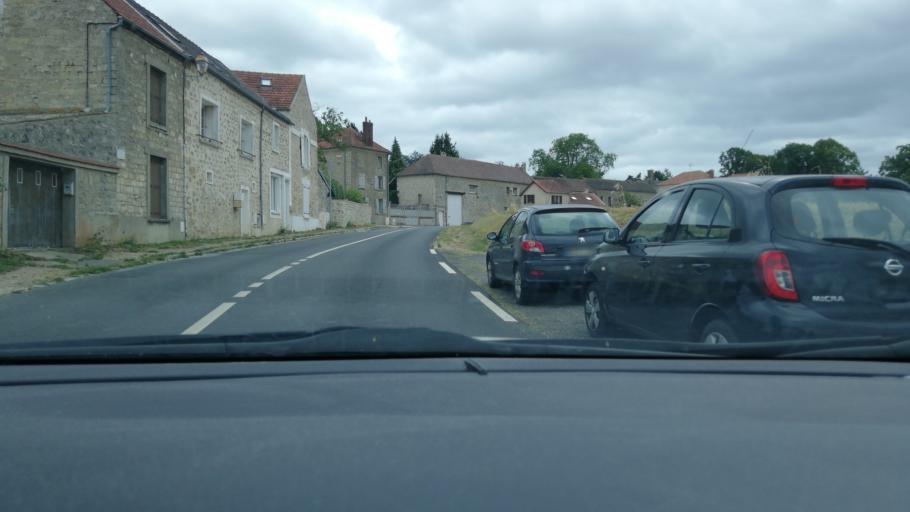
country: FR
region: Ile-de-France
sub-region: Departement du Val-d'Oise
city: Ennery
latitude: 49.1037
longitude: 2.1326
